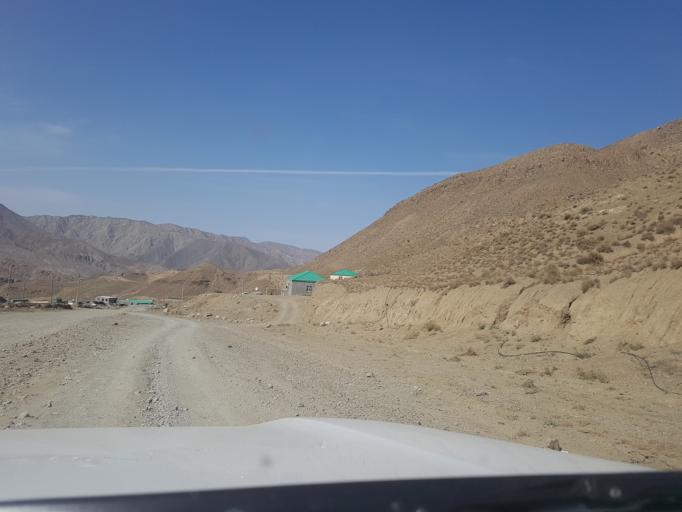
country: TM
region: Ahal
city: Baharly
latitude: 38.4515
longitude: 57.0463
